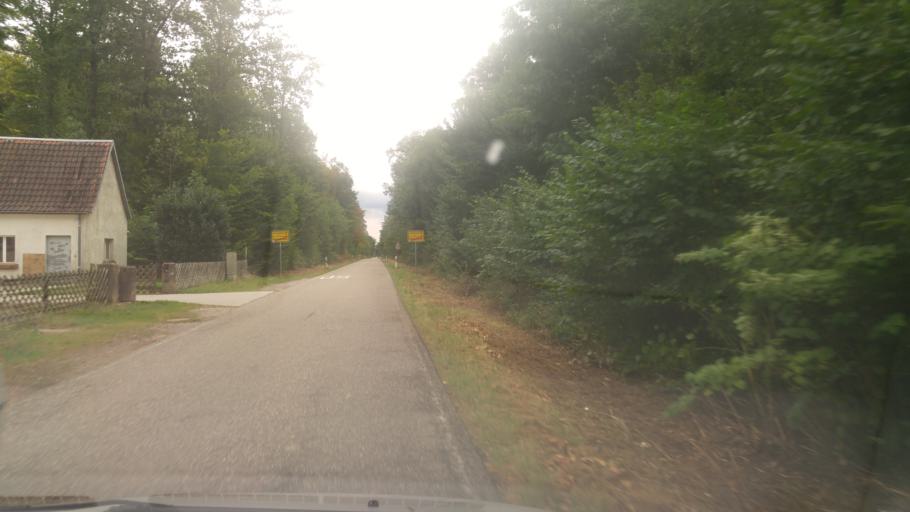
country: DE
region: Rheinland-Pfalz
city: Steinfeld
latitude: 48.9986
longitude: 8.0751
